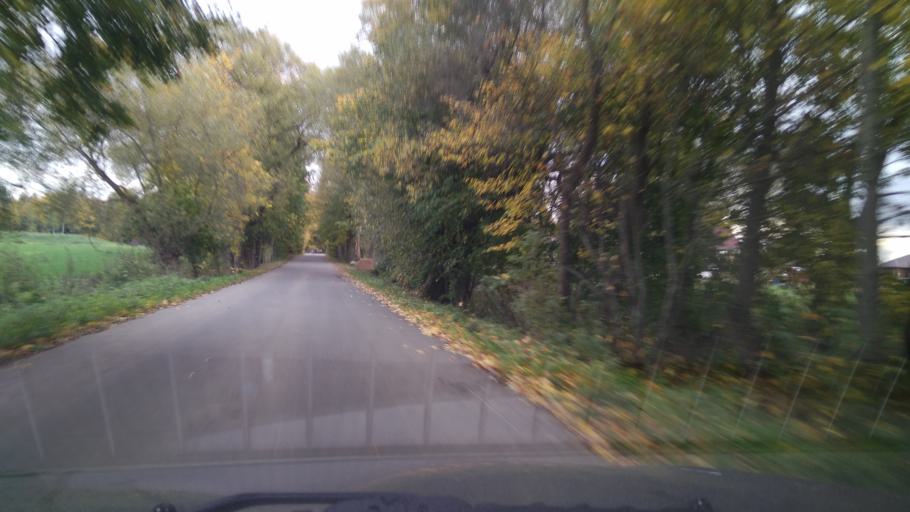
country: BY
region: Minsk
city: Dukora
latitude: 53.6790
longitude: 27.9602
